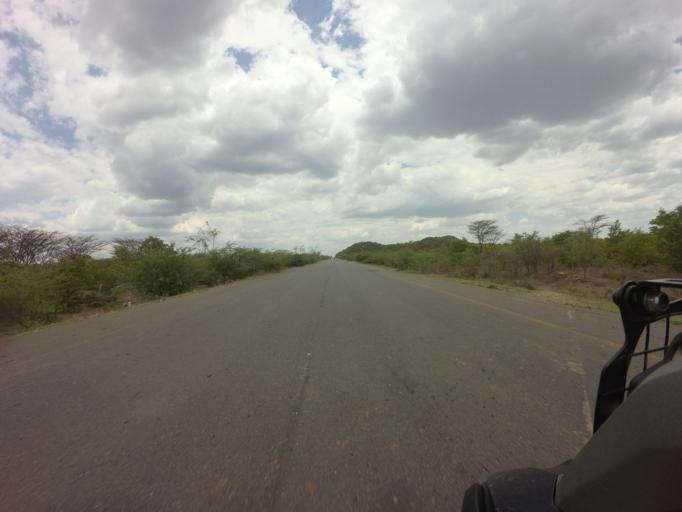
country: AO
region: Huila
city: Lubango
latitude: -15.3024
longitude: 13.8342
